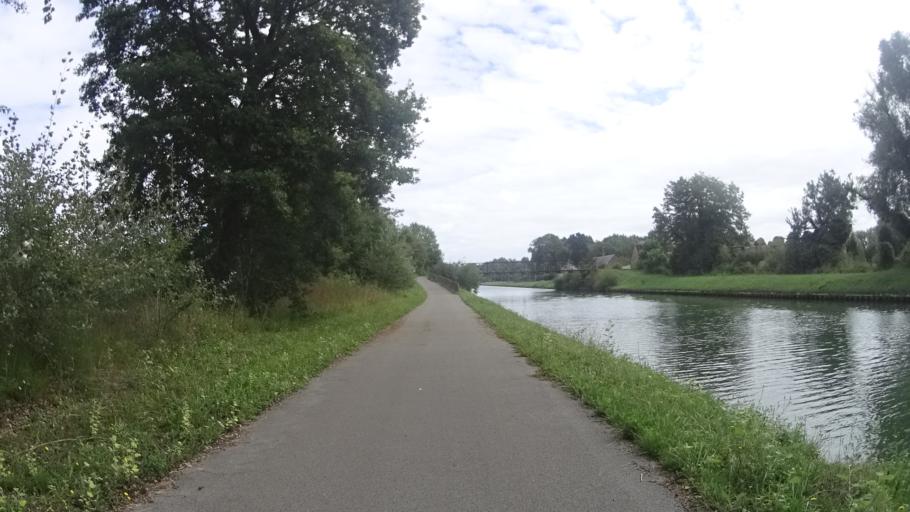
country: FR
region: Picardie
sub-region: Departement de l'Oise
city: Crisolles
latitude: 49.5777
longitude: 3.0802
